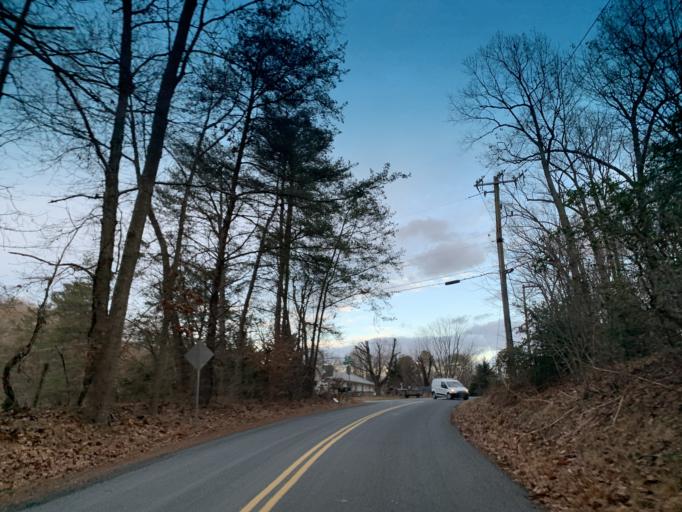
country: US
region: Pennsylvania
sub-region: York County
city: Susquehanna Trails
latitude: 39.6562
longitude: -76.3001
